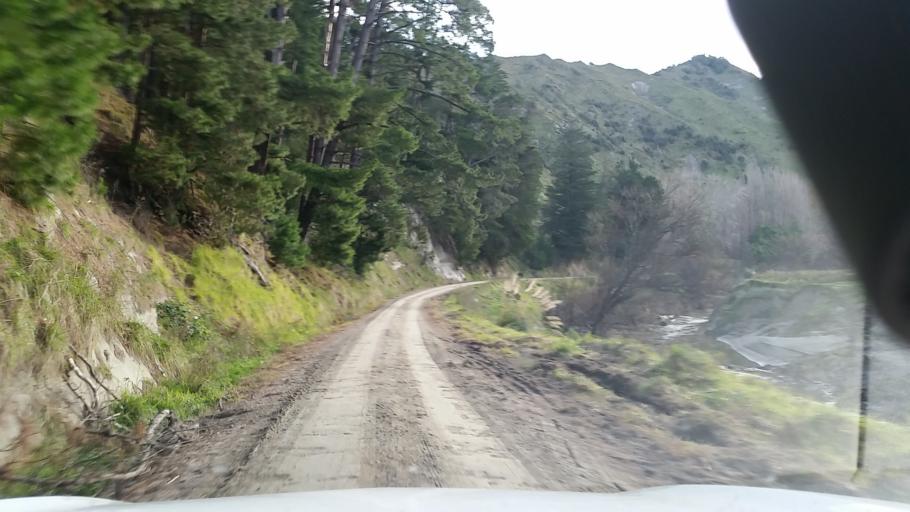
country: NZ
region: Taranaki
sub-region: South Taranaki District
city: Patea
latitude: -39.5651
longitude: 174.8087
